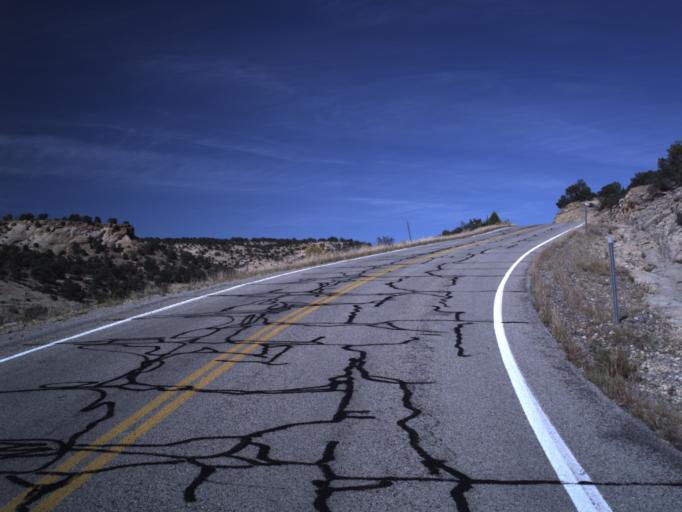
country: US
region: Utah
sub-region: San Juan County
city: Monticello
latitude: 37.9873
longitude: -109.4976
